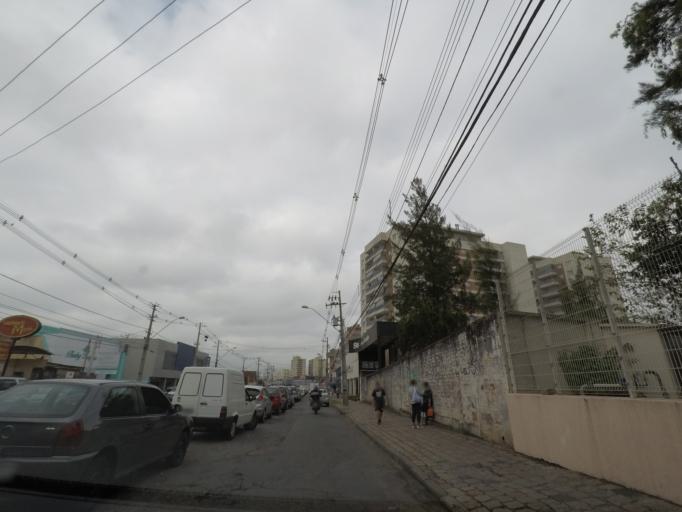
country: BR
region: Parana
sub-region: Curitiba
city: Curitiba
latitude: -25.4853
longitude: -49.2941
